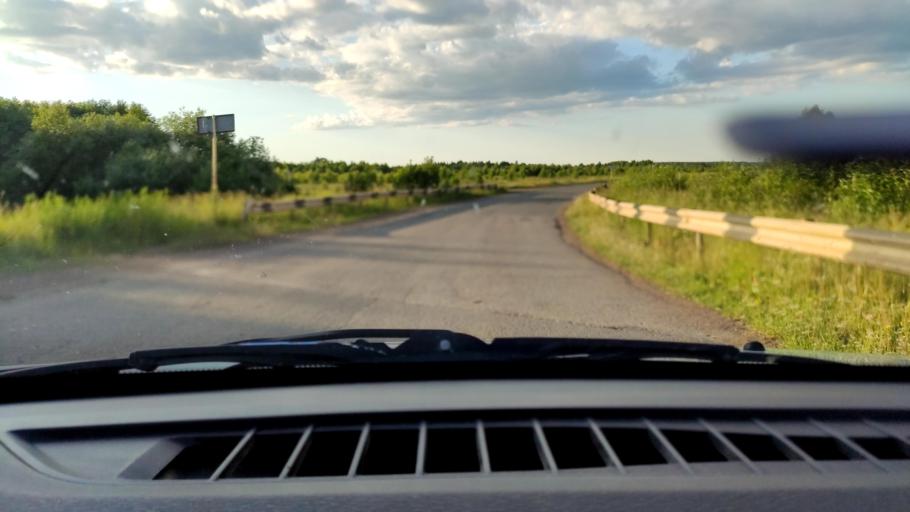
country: RU
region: Perm
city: Uinskoye
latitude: 57.0811
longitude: 56.5537
